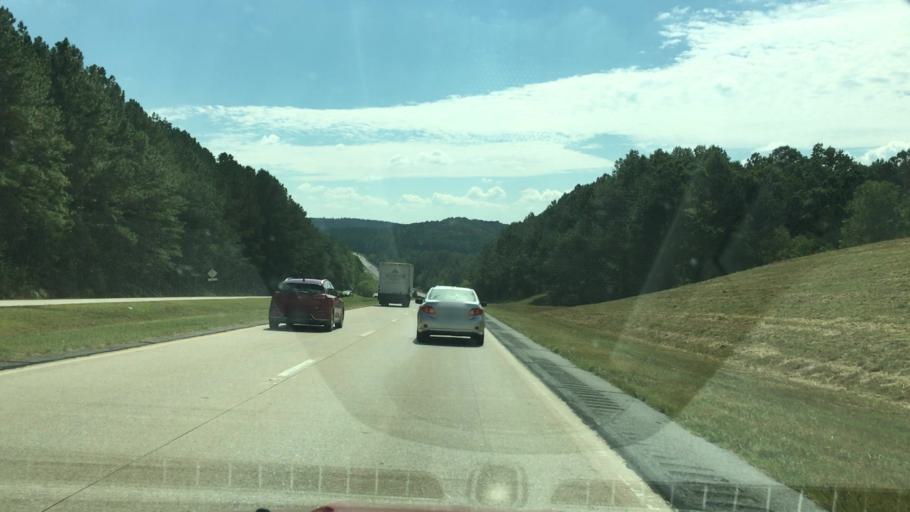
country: US
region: Georgia
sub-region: Pickens County
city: Jasper
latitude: 34.5267
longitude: -84.5173
